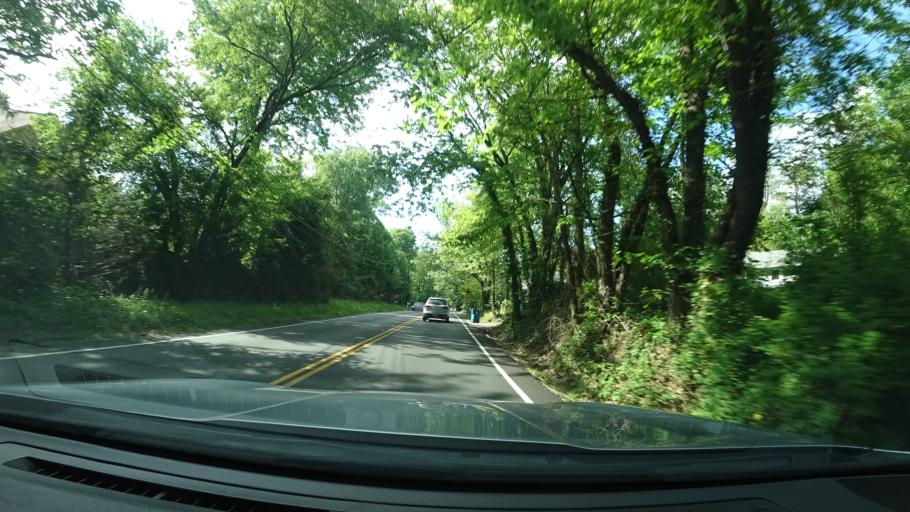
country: US
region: Virginia
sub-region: Fairfax County
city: McLean
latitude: 38.9250
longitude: -77.1651
